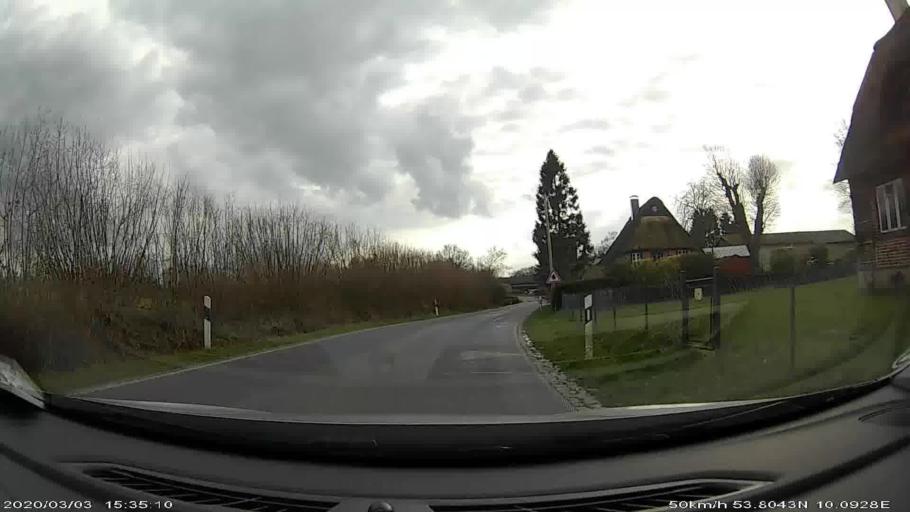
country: DE
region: Schleswig-Holstein
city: Huttblek
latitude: 53.8050
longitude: 10.0926
